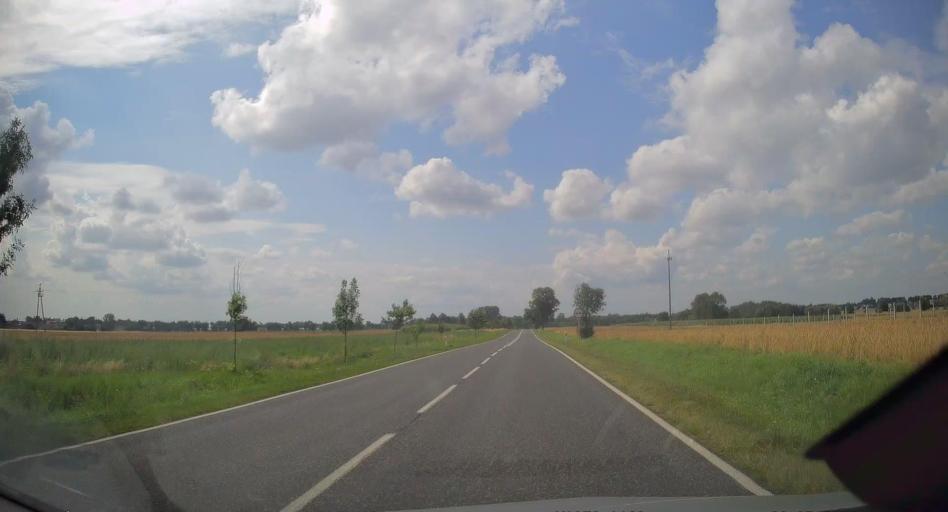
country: PL
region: Lodz Voivodeship
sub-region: Powiat brzezinski
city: Jezow
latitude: 51.8002
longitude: 20.0228
